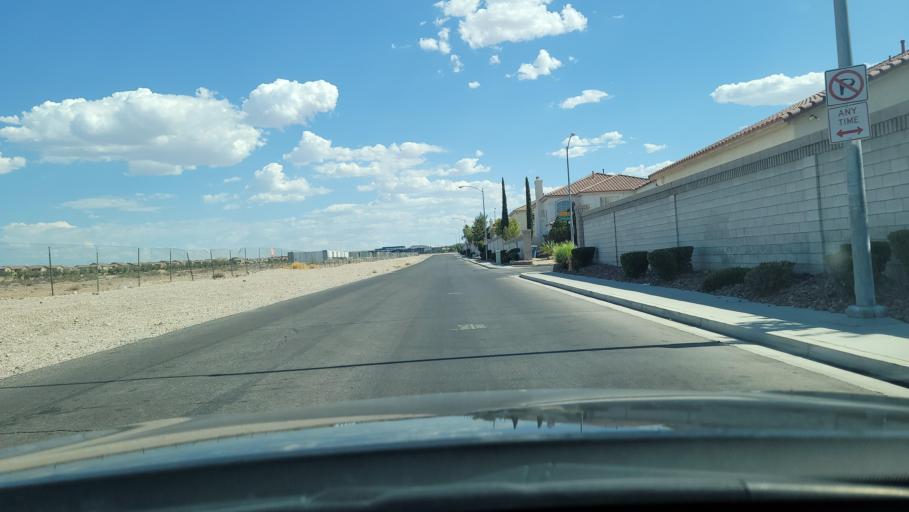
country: US
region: Nevada
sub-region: Clark County
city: Spring Valley
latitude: 36.0807
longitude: -115.2724
